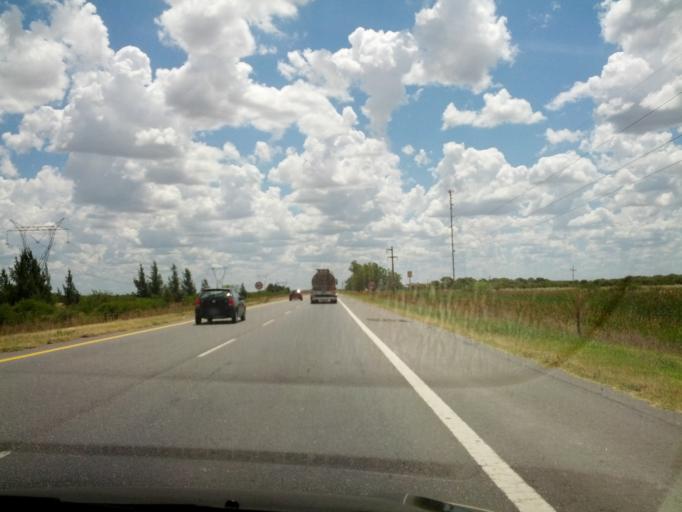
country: AR
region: Entre Rios
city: Ceibas
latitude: -33.4607
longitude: -58.8026
